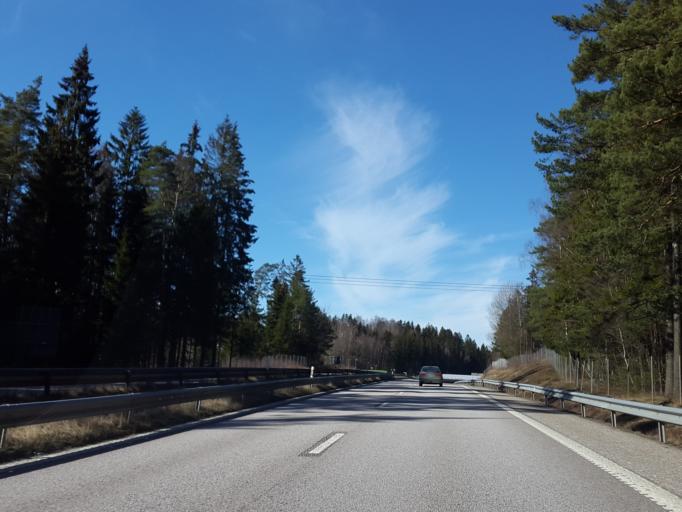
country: SE
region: Vaestra Goetaland
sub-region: Alingsas Kommun
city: Ingared
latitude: 57.8818
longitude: 12.4921
